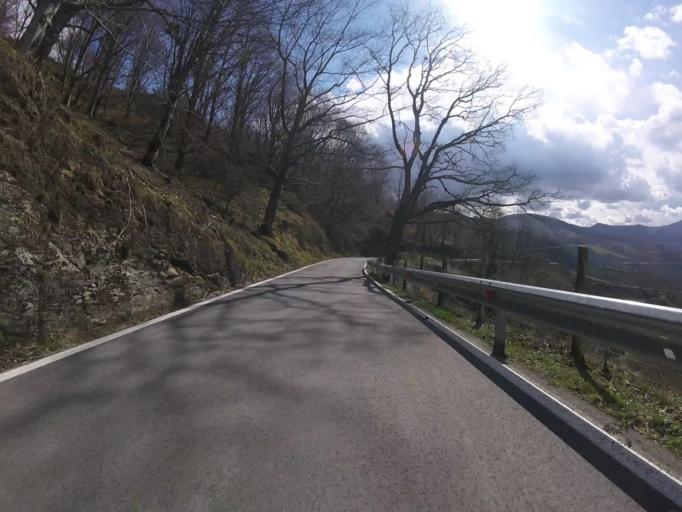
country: ES
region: Navarre
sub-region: Provincia de Navarra
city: Etxalar
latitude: 43.2555
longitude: -1.6180
